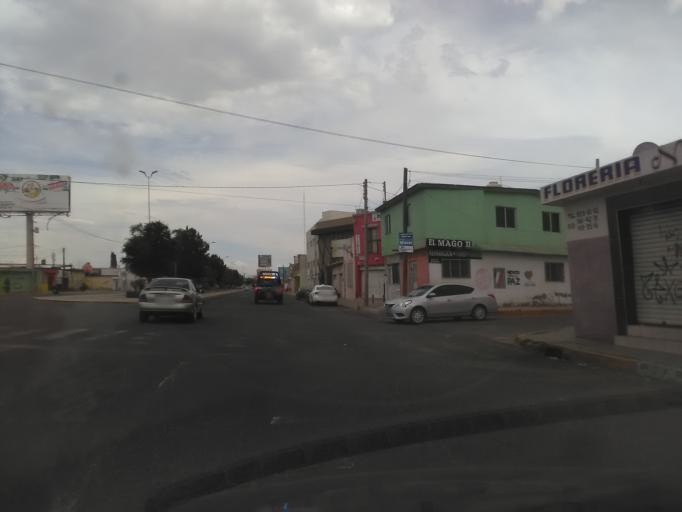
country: MX
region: Durango
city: Victoria de Durango
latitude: 24.0164
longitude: -104.6484
